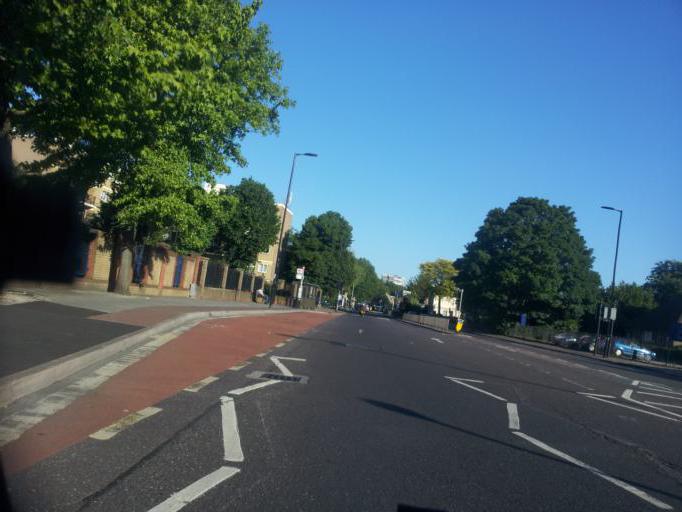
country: GB
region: England
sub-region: Greater London
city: Bethnal Green
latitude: 51.4984
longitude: -0.0548
